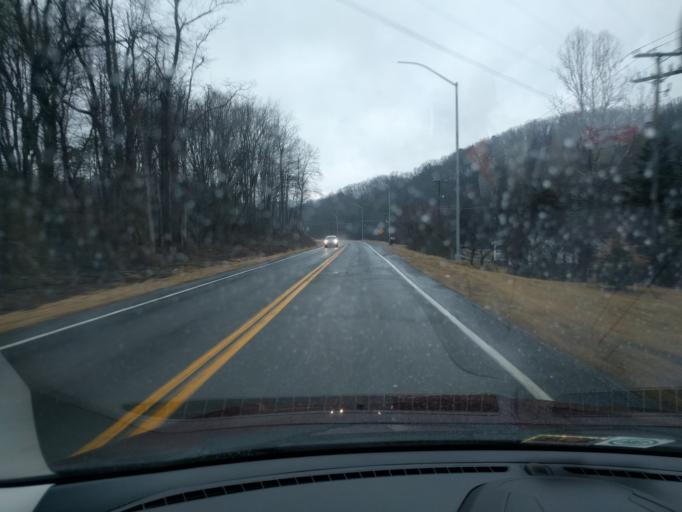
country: US
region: Virginia
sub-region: Pulaski County
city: Pulaski
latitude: 37.0387
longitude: -80.7372
